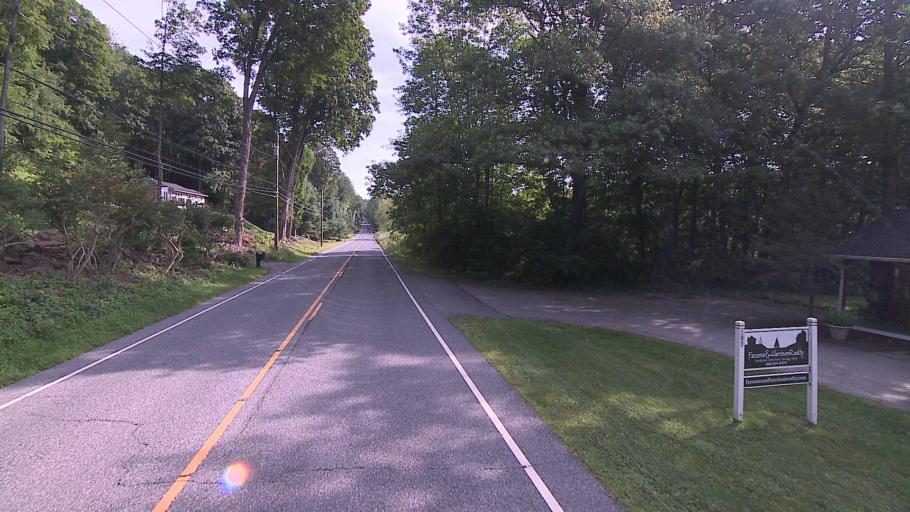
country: US
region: Connecticut
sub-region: Fairfield County
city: Sherman
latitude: 41.5291
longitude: -73.5101
